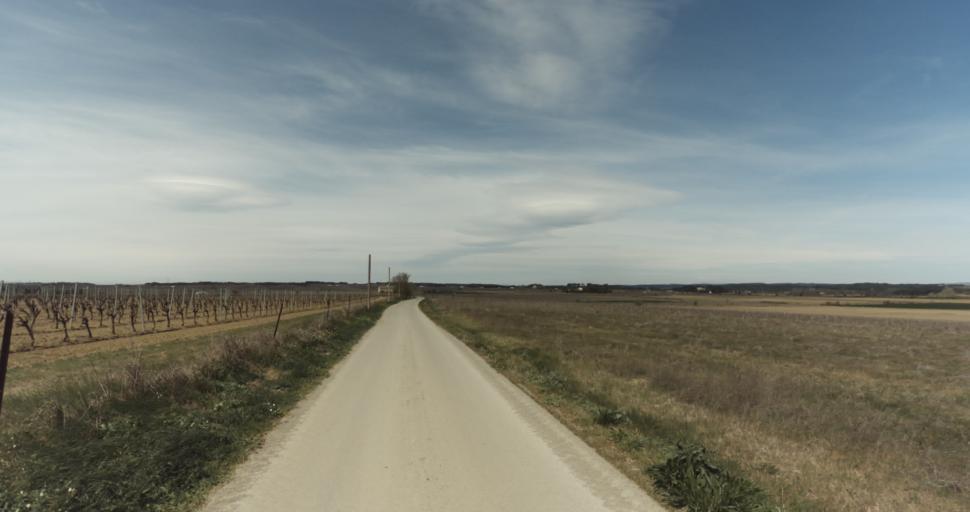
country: FR
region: Languedoc-Roussillon
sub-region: Departement de l'Herault
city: Pinet
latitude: 43.4070
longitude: 3.5492
